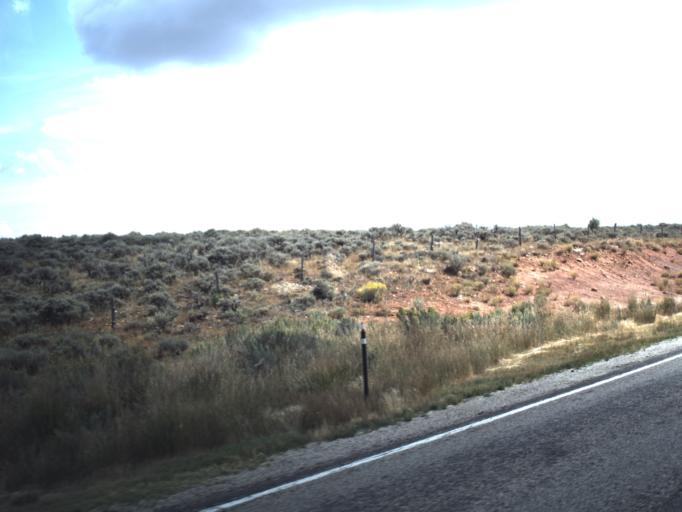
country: US
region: Utah
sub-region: Rich County
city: Randolph
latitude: 41.8038
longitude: -111.2465
